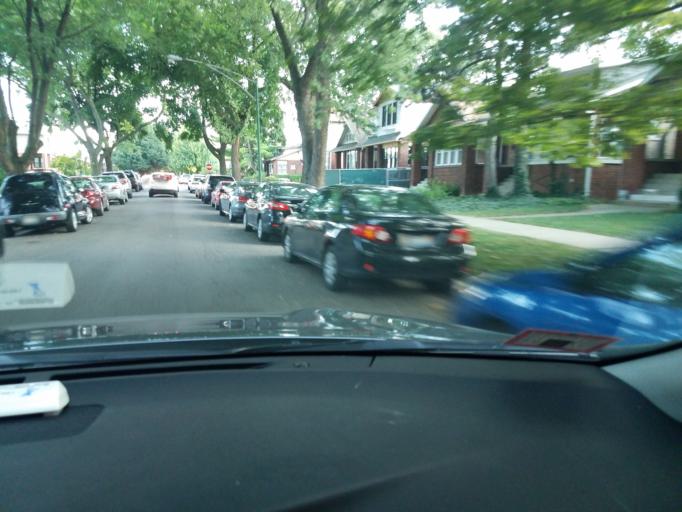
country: US
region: Illinois
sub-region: Cook County
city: Lincolnwood
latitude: 41.9652
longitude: -87.7371
